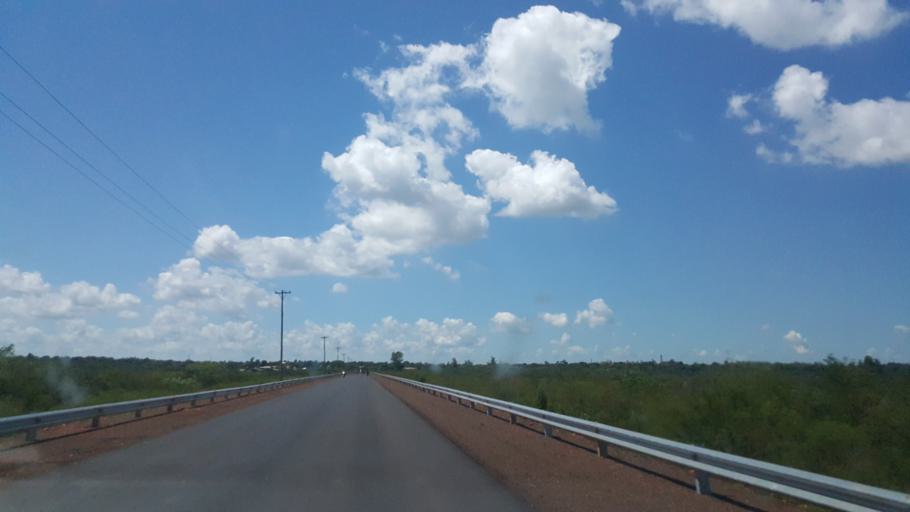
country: AR
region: Corrientes
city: Santo Tome
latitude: -28.5326
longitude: -56.0528
